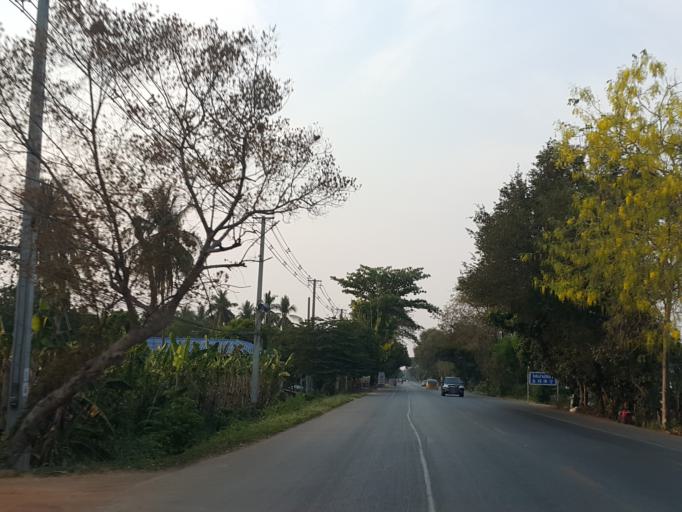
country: TH
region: Sukhothai
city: Si Samrong
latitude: 17.2404
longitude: 99.8582
